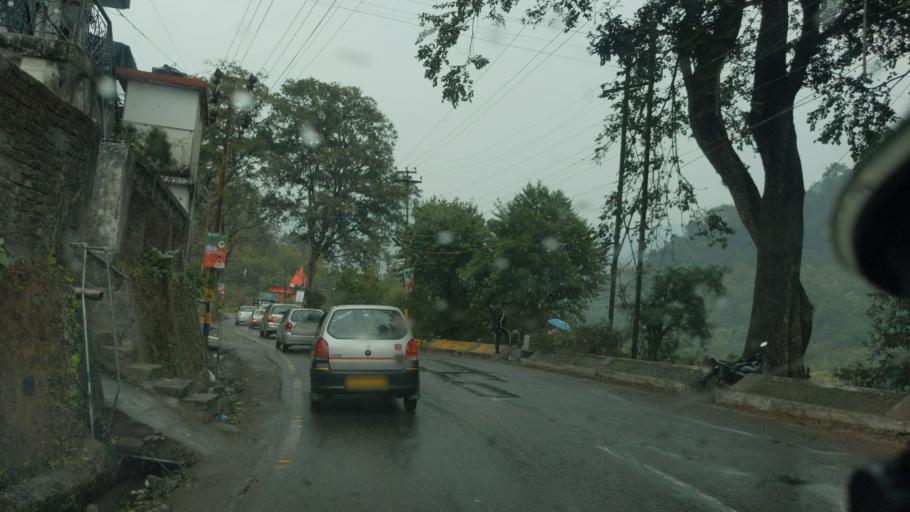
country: IN
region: Uttarakhand
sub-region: Naini Tal
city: Haldwani
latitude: 29.2752
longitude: 79.5455
